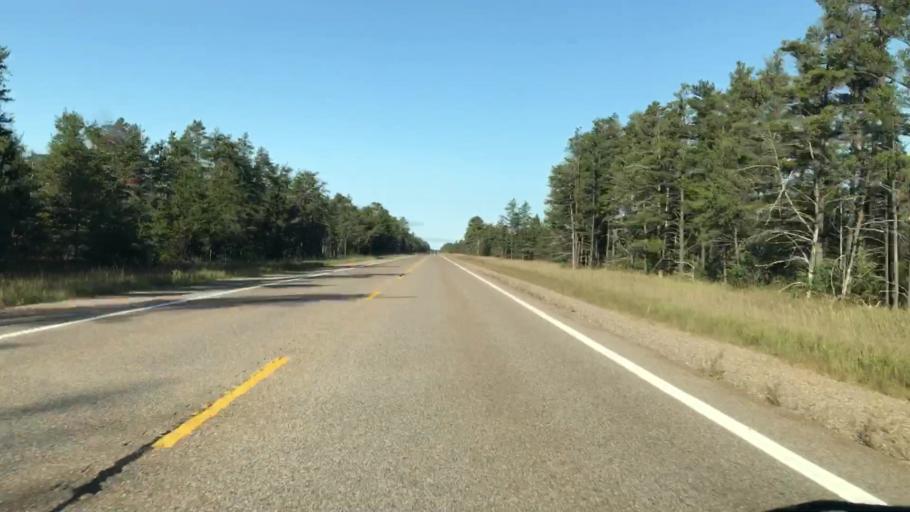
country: US
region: Michigan
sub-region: Mackinac County
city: Saint Ignace
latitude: 46.3586
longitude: -84.8369
